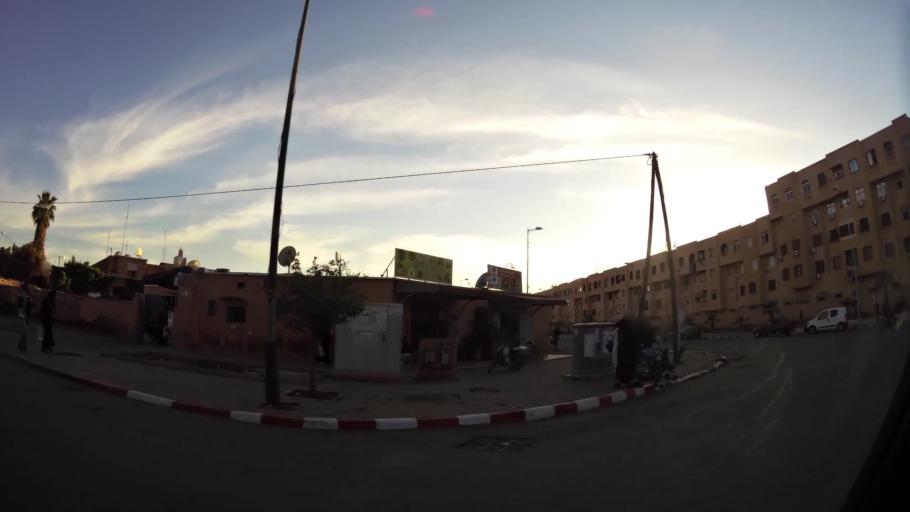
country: MA
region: Marrakech-Tensift-Al Haouz
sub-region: Marrakech
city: Marrakesh
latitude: 31.6206
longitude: -8.0271
